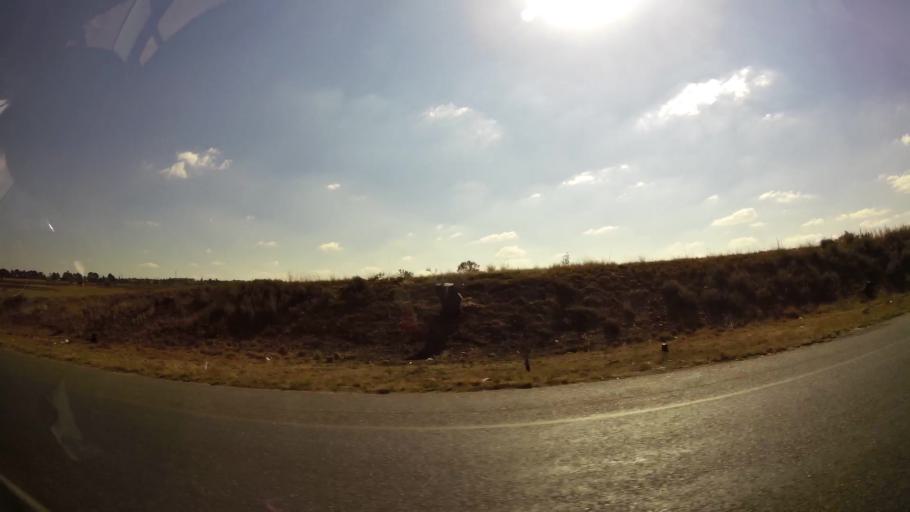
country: ZA
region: Gauteng
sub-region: West Rand District Municipality
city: Randfontein
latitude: -26.1769
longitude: 27.7677
